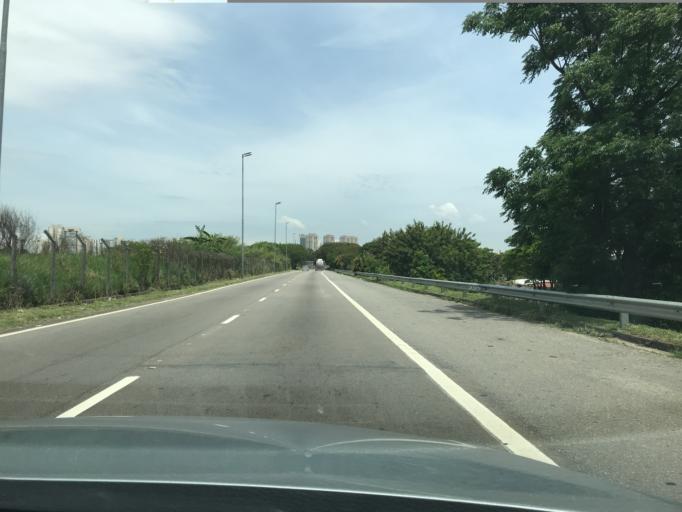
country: BR
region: Sao Paulo
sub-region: Osasco
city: Osasco
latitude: -23.5125
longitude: -46.7379
